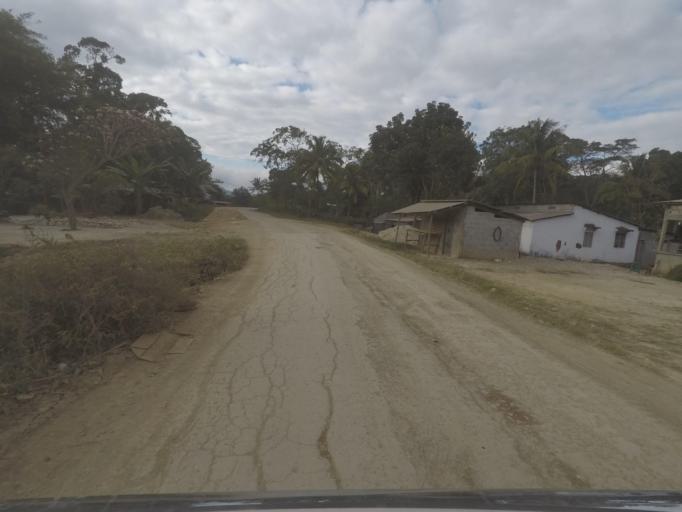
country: TL
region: Baucau
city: Venilale
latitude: -8.6095
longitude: 126.3822
